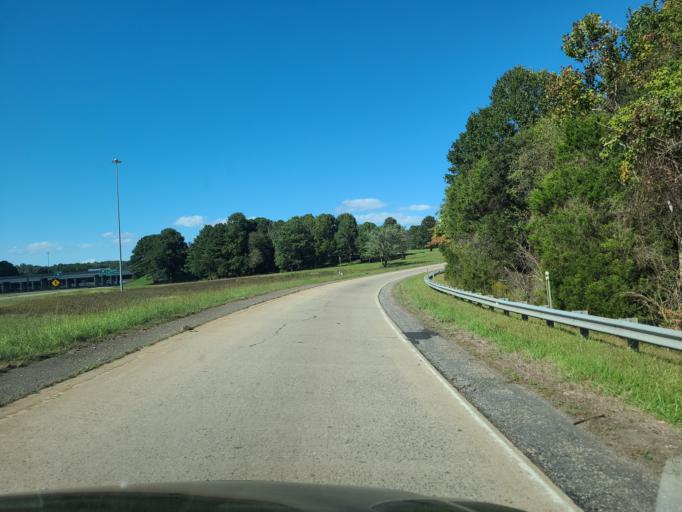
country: US
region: North Carolina
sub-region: Catawba County
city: Mountain View
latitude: 35.7051
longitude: -81.3515
